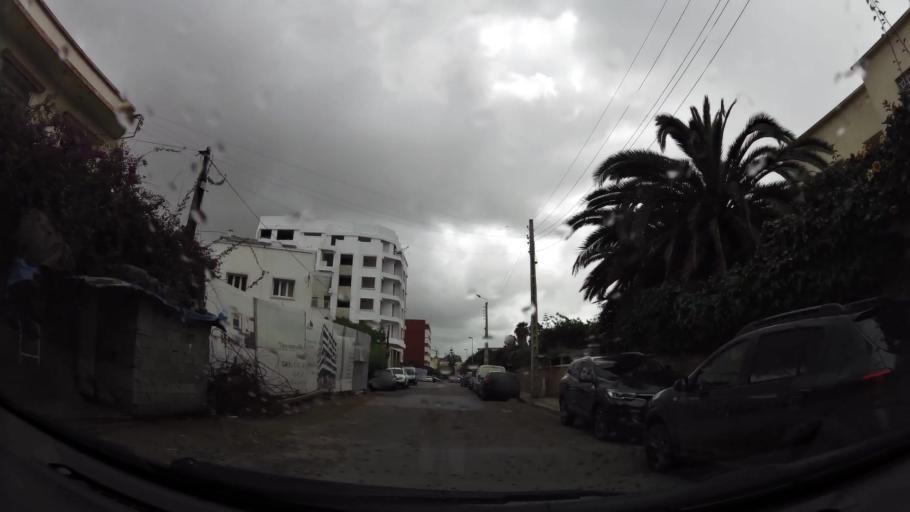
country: MA
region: Grand Casablanca
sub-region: Casablanca
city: Casablanca
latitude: 33.5710
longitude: -7.6191
